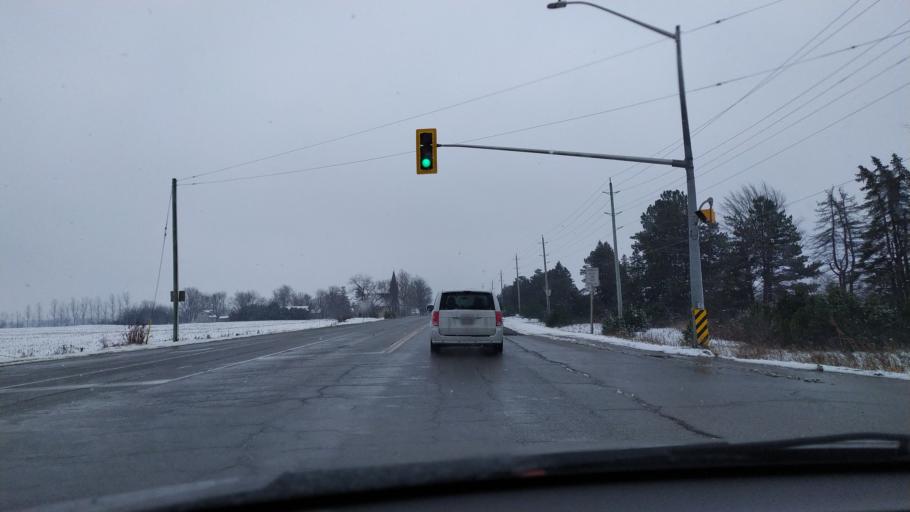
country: CA
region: Ontario
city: Waterloo
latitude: 43.6239
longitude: -80.6951
